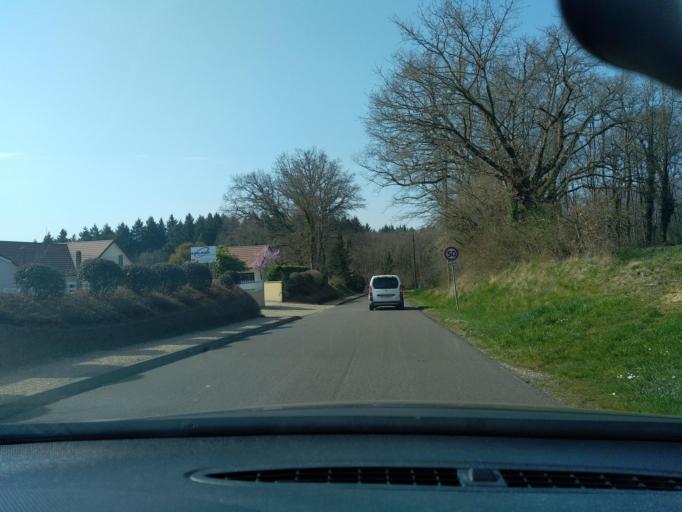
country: FR
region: Franche-Comte
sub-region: Departement du Jura
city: Dole
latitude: 47.0441
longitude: 5.5214
